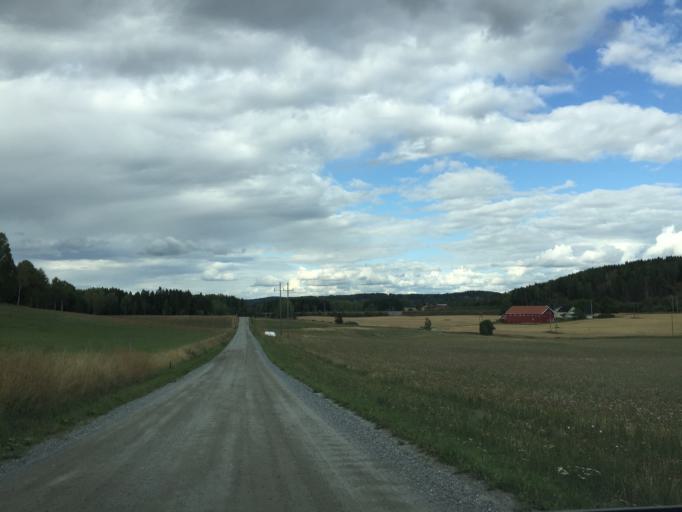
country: NO
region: Ostfold
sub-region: Askim
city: Askim
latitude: 59.5962
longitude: 11.1346
